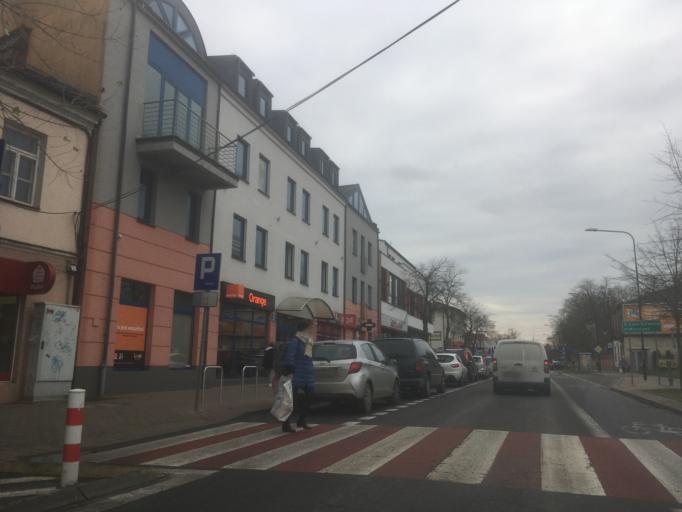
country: PL
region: Masovian Voivodeship
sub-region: Powiat piaseczynski
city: Piaseczno
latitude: 52.0700
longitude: 21.0269
